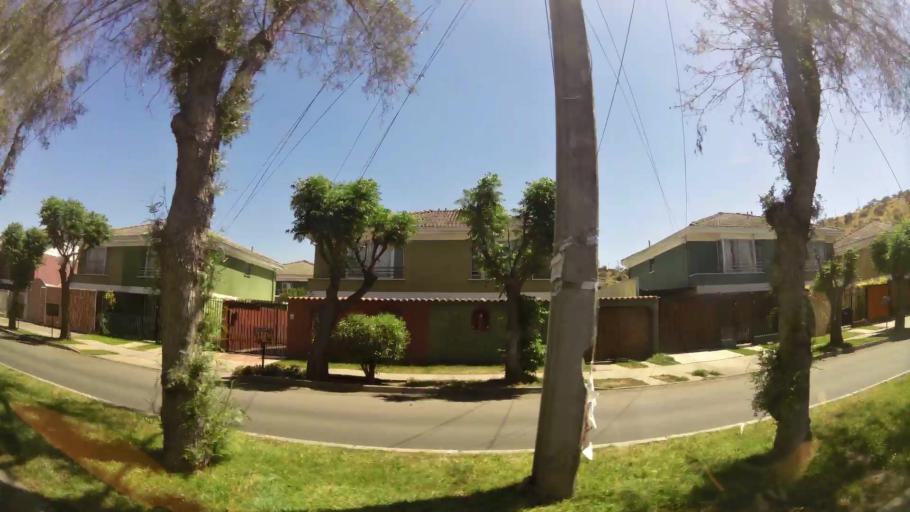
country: CL
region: Santiago Metropolitan
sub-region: Provincia de Maipo
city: San Bernardo
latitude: -33.6224
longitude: -70.7090
